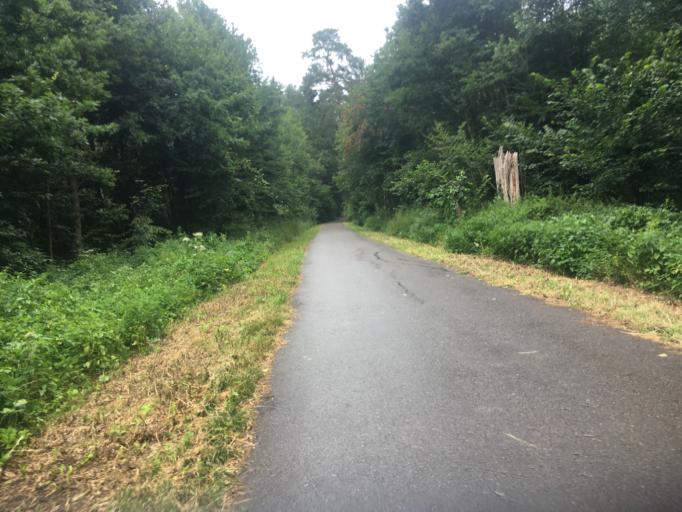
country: CH
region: Fribourg
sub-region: See District
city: Bas-Vully
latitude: 46.9775
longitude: 7.0934
